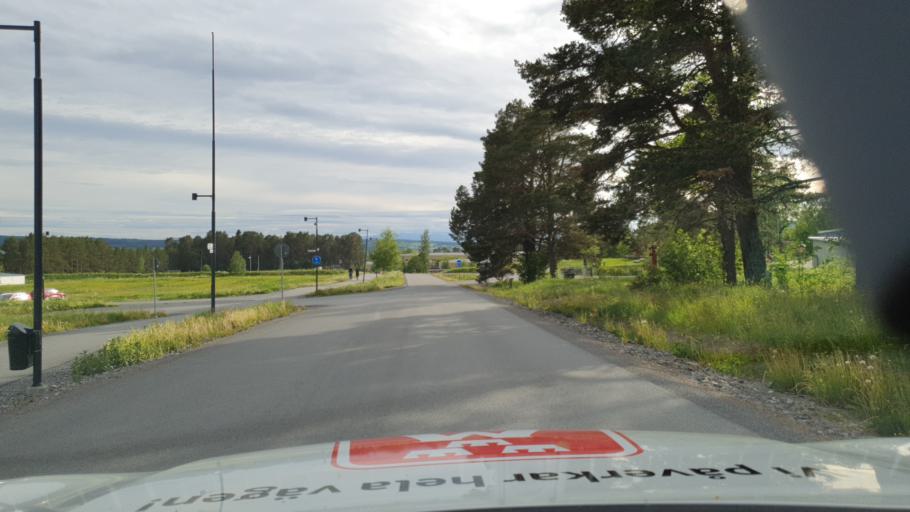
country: SE
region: Jaemtland
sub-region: OEstersunds Kommun
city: Ostersund
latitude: 63.1804
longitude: 14.6706
